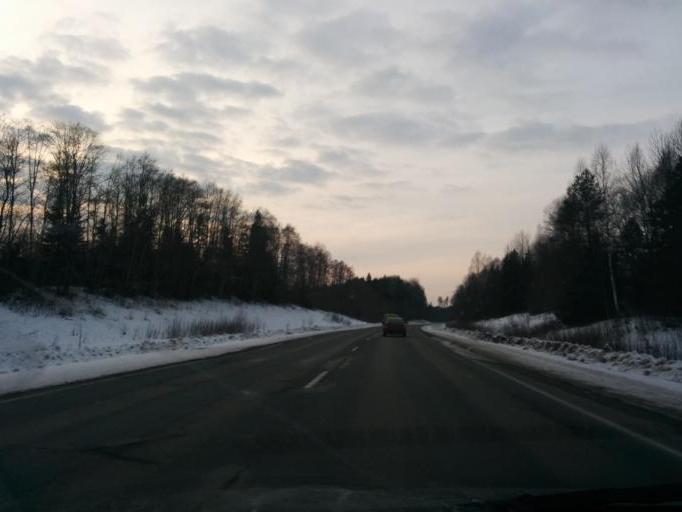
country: LV
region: Raunas
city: Rauna
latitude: 57.3154
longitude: 25.7245
